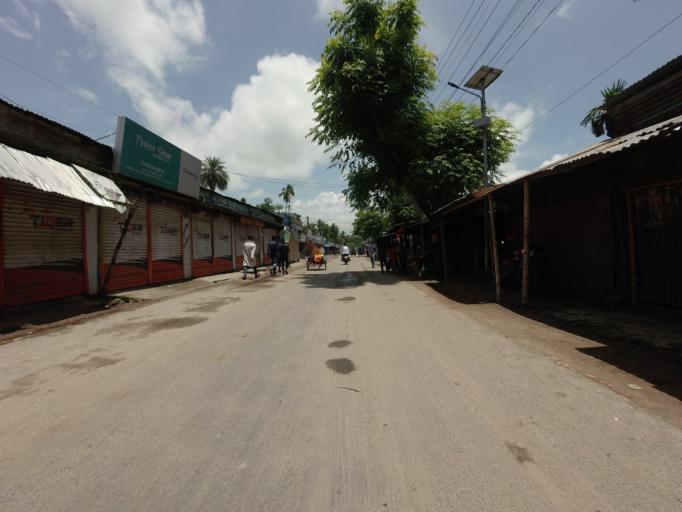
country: BD
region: Khulna
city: Kalia
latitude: 23.0386
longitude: 89.6324
